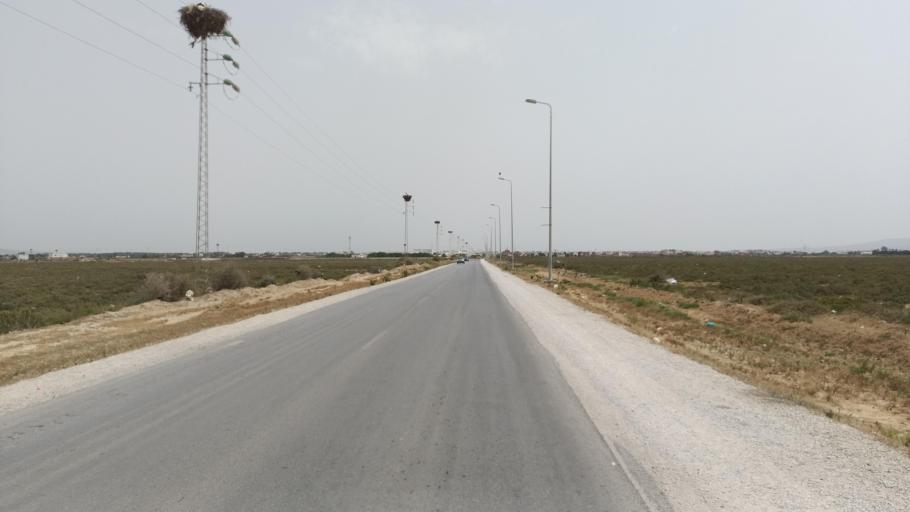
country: TN
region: Nabul
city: Manzil Bu Zalafah
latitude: 36.7188
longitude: 10.4760
